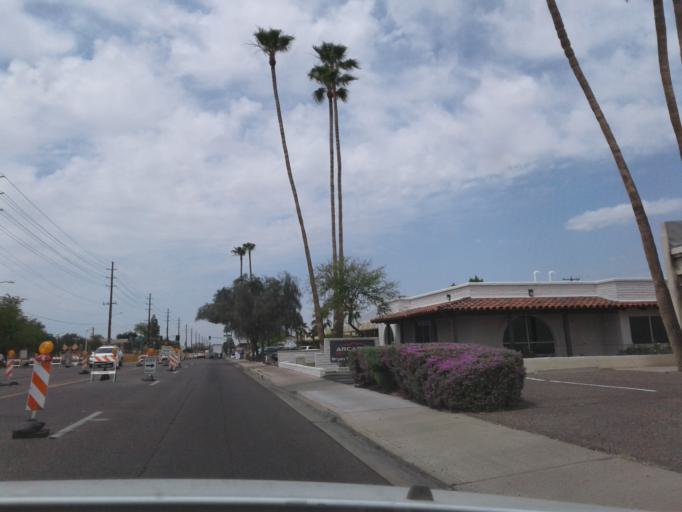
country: US
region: Arizona
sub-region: Maricopa County
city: Paradise Valley
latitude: 33.4801
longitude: -111.9590
